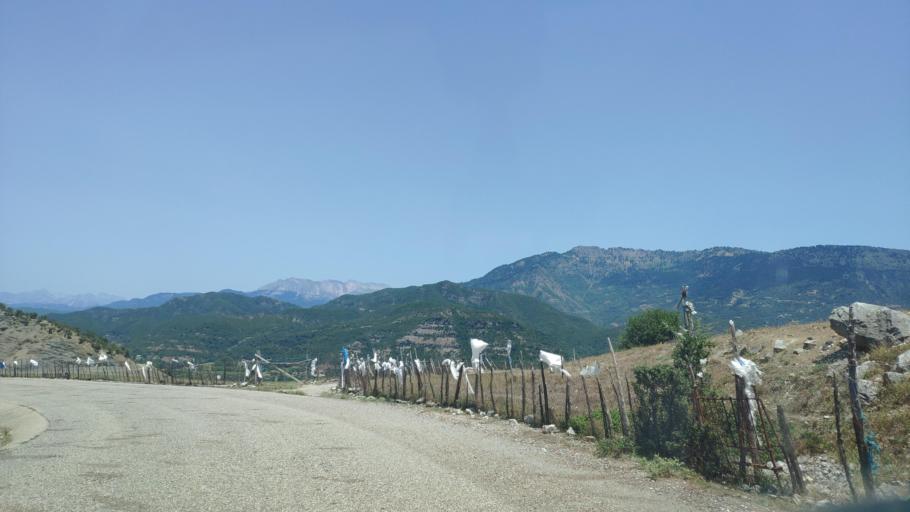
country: GR
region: Thessaly
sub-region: Nomos Kardhitsas
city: Anthiro
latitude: 39.1538
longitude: 21.3855
